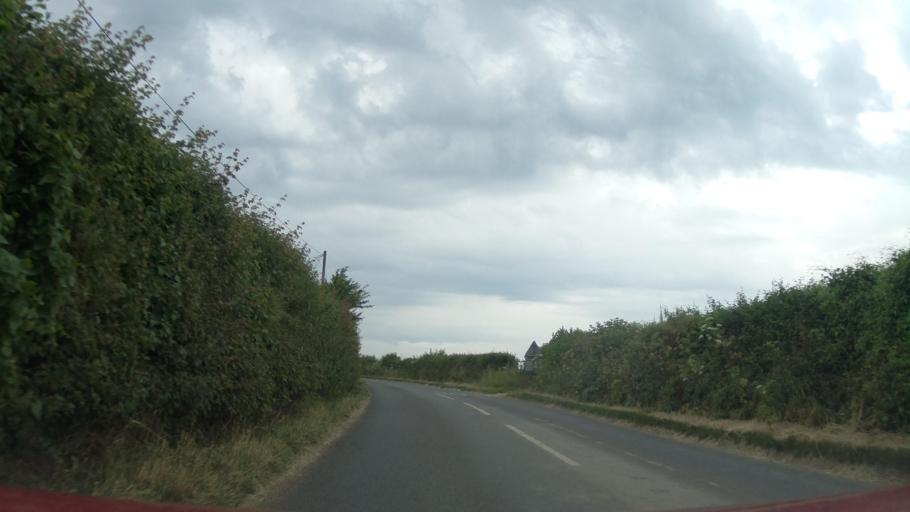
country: GB
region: England
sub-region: Dorset
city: Sherborne
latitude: 50.9274
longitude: -2.5399
